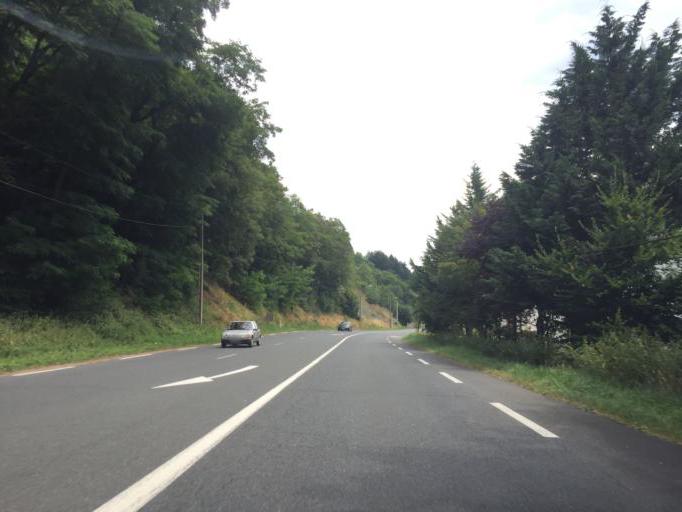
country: FR
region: Rhone-Alpes
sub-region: Departement du Rhone
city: Tarare
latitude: 45.8927
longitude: 4.4048
